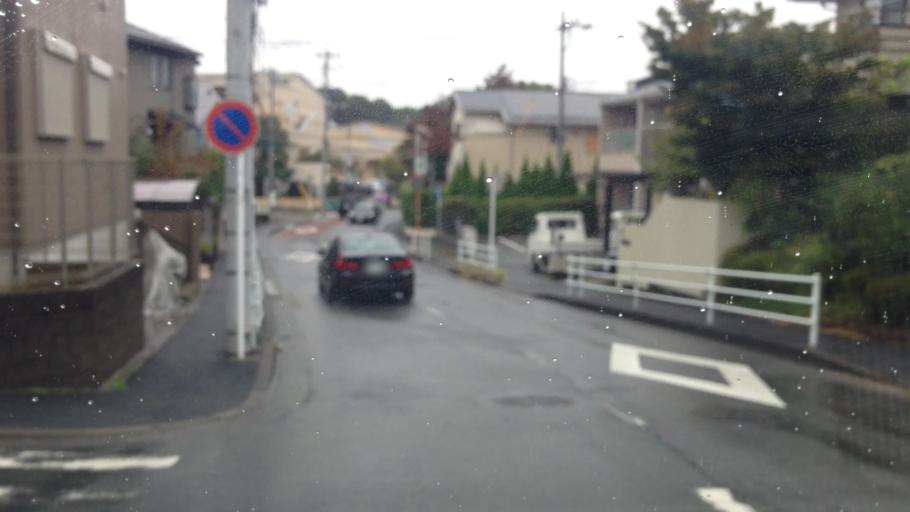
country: JP
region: Kanagawa
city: Yokohama
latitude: 35.5422
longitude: 139.5825
